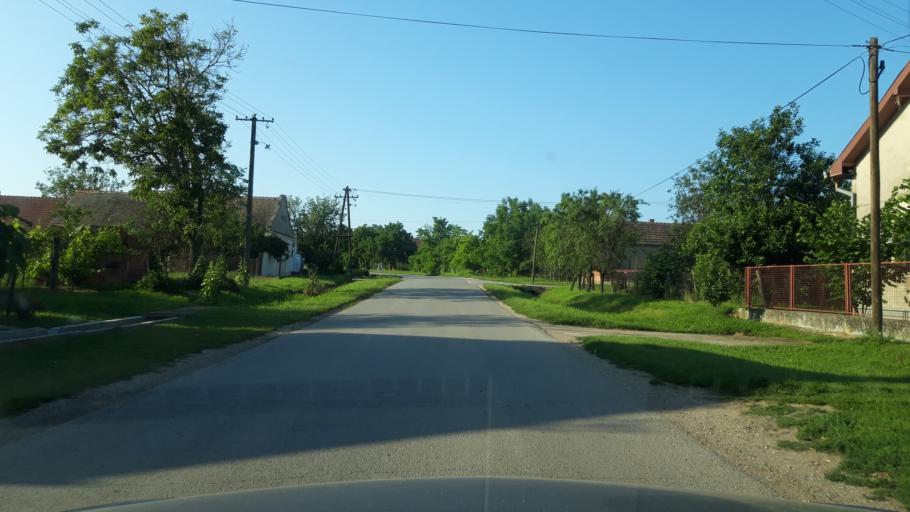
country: RS
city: Celarevo
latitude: 45.1150
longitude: 19.5091
